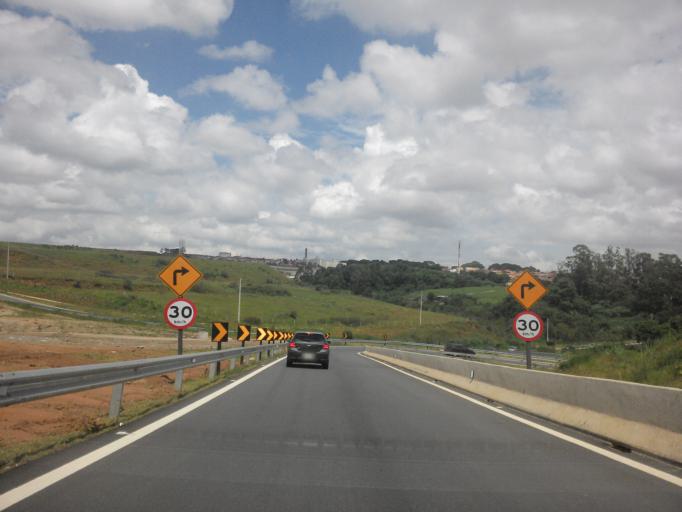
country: BR
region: Sao Paulo
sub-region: Campinas
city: Campinas
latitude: -22.8672
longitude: -47.0214
